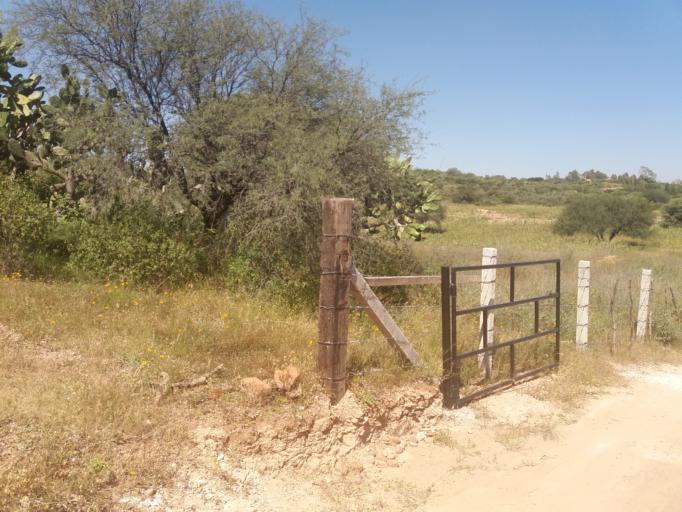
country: MX
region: Aguascalientes
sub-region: Aguascalientes
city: San Sebastian [Fraccionamiento]
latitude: 21.7759
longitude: -102.2336
